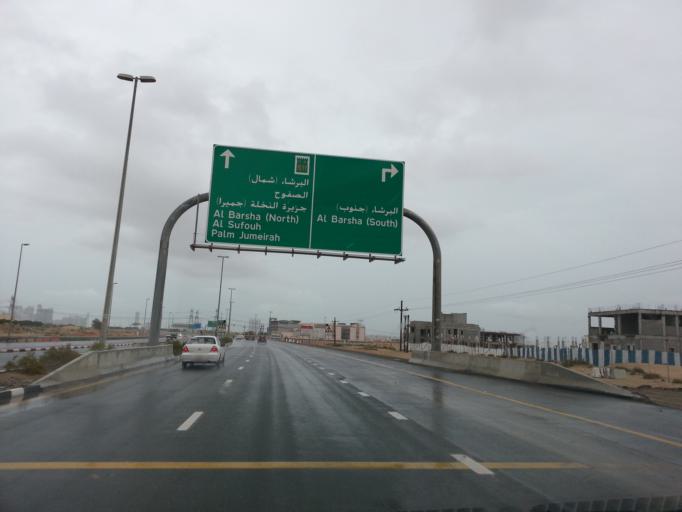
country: AE
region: Dubai
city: Dubai
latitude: 25.0690
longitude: 55.2184
